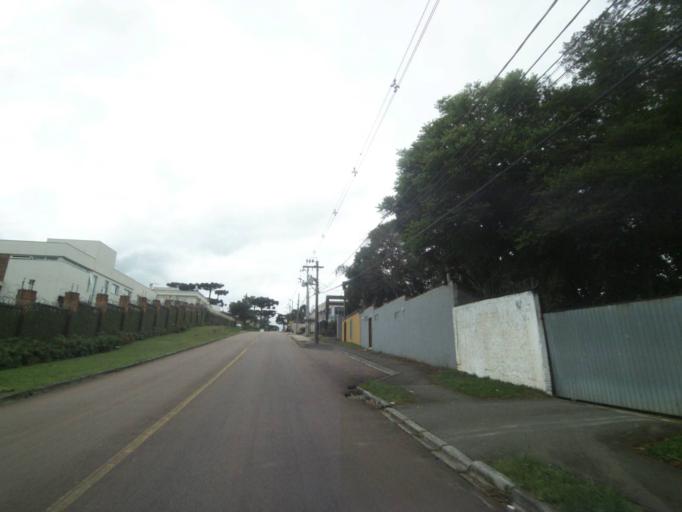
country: BR
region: Parana
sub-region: Curitiba
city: Curitiba
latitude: -25.4591
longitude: -49.3372
